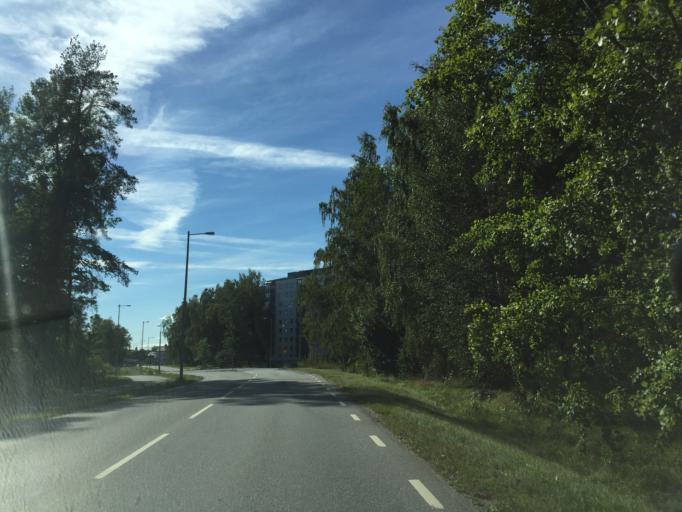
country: SE
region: OErebro
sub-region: Orebro Kommun
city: Orebro
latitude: 59.2874
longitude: 15.2402
